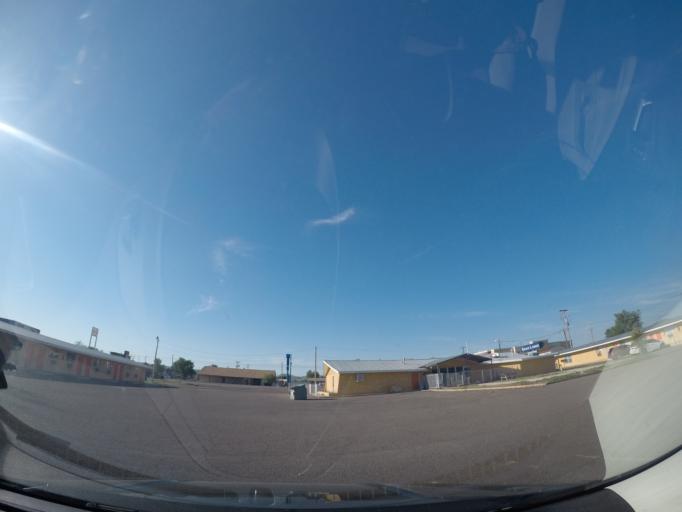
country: US
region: Texas
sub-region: Brewster County
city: Alpine
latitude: 30.3654
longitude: -103.6400
